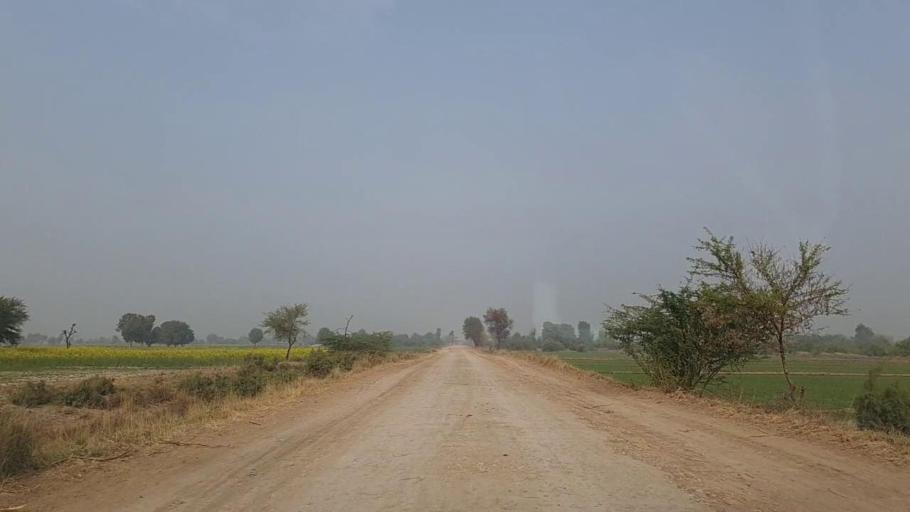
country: PK
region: Sindh
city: Sanghar
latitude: 26.0928
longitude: 68.8983
